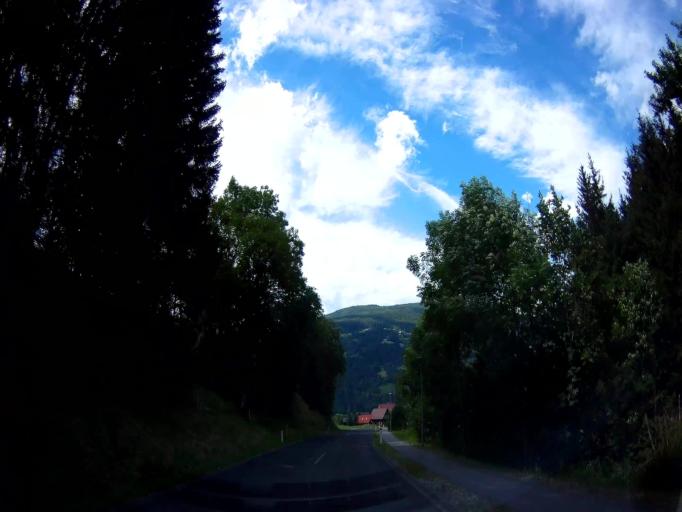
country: AT
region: Styria
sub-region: Politischer Bezirk Murau
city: Stadl an der Mur
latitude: 47.0754
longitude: 13.9832
